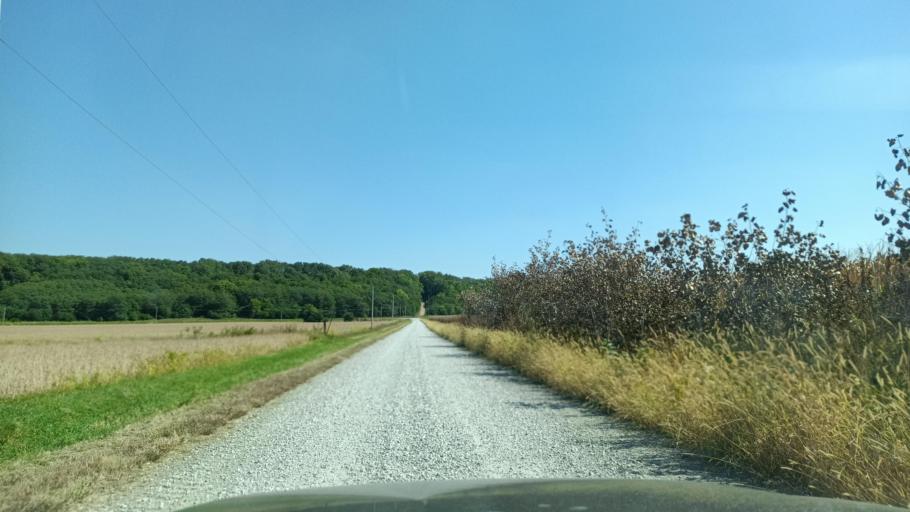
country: US
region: Illinois
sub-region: Mercer County
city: Aledo
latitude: 41.1645
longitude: -90.9191
